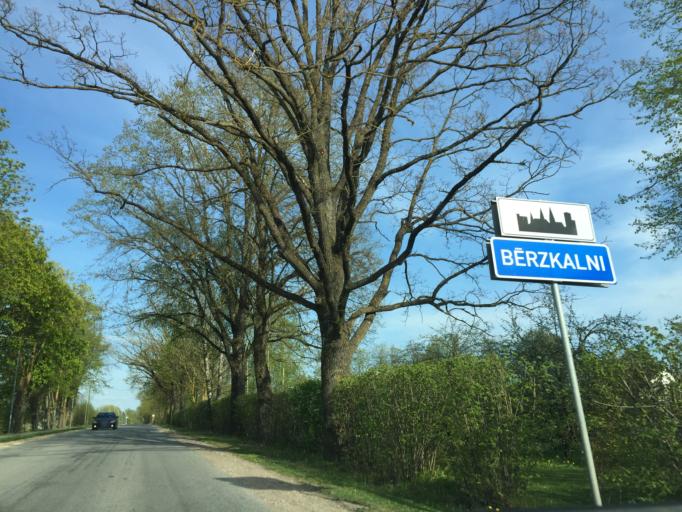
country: LV
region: Bauskas Rajons
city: Bauska
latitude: 56.3994
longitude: 24.1816
